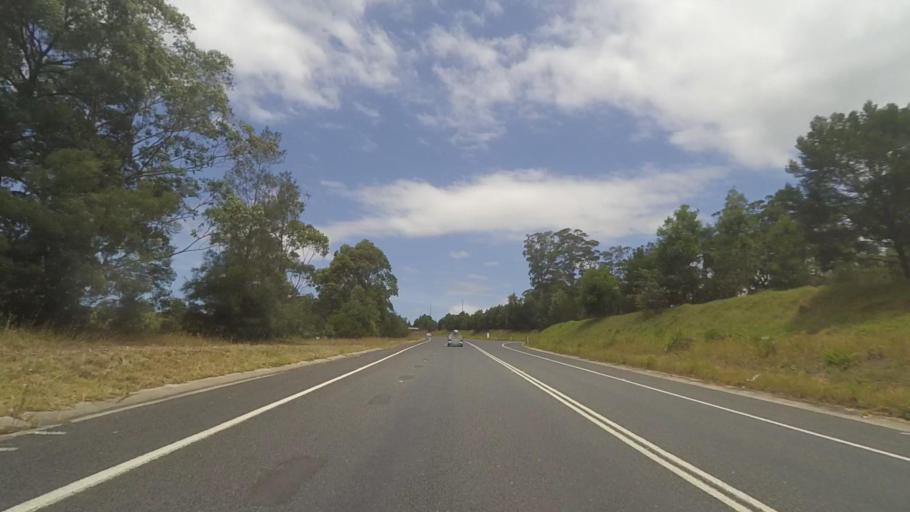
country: AU
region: New South Wales
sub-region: Shoalhaven Shire
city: Milton
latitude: -35.2181
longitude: 150.4348
